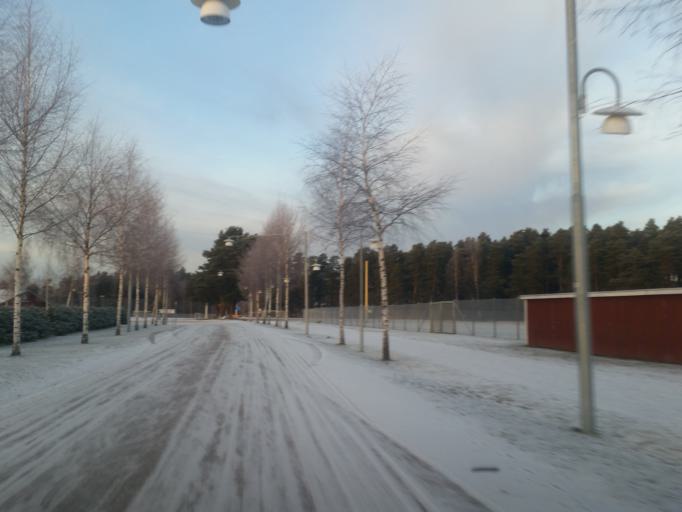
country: SE
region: Dalarna
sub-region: Leksand Municipality
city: Leksand
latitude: 60.7359
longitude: 14.9831
